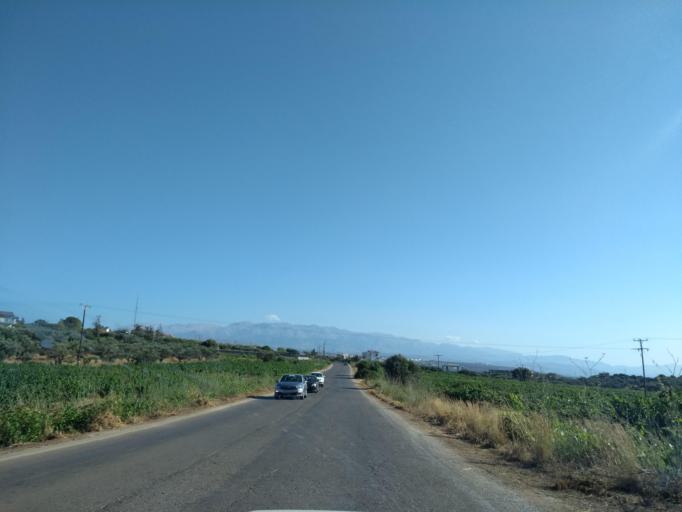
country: GR
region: Crete
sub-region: Nomos Chanias
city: Pithari
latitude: 35.5755
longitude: 24.0926
